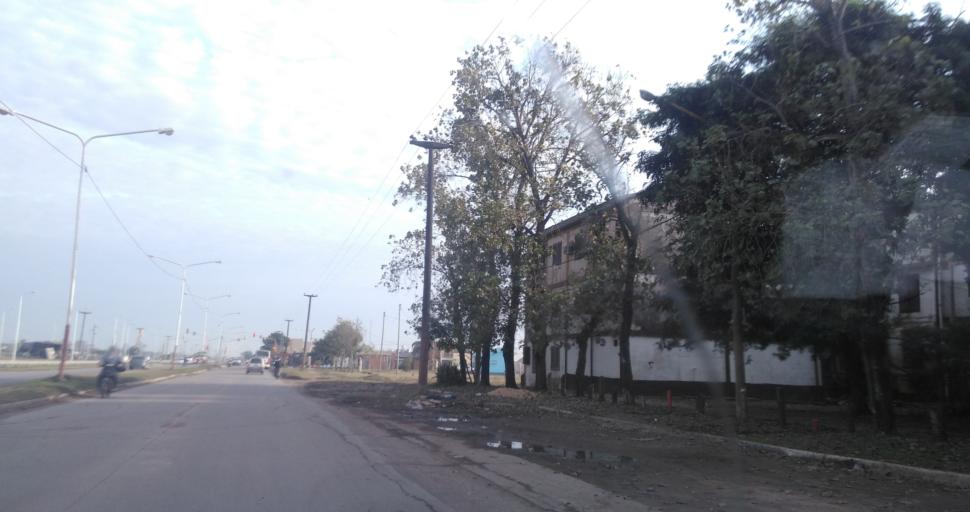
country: AR
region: Chaco
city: Resistencia
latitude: -27.4677
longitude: -59.0109
